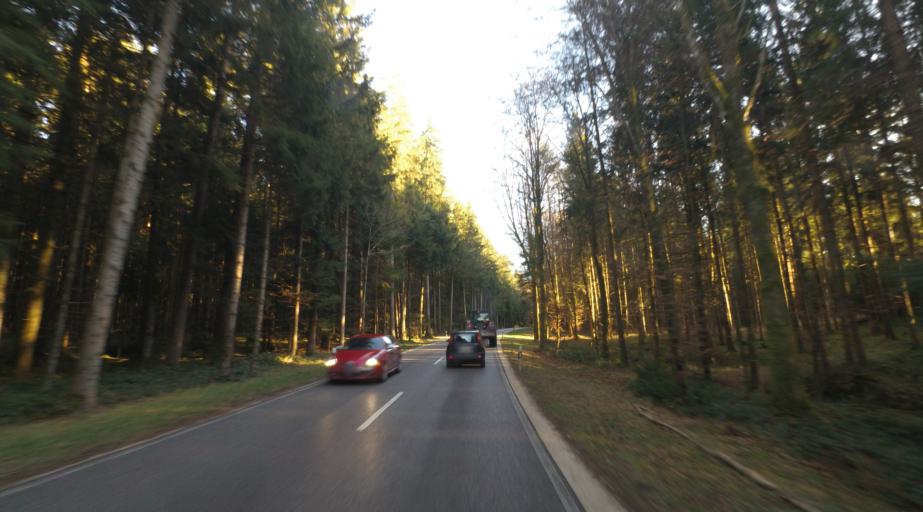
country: DE
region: Bavaria
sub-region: Upper Bavaria
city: Palling
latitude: 48.0054
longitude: 12.6253
